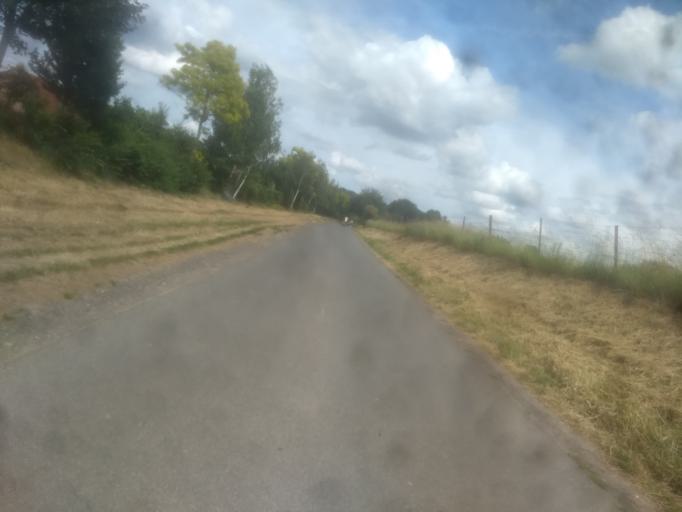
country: FR
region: Nord-Pas-de-Calais
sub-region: Departement du Pas-de-Calais
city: Duisans
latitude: 50.3043
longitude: 2.6834
